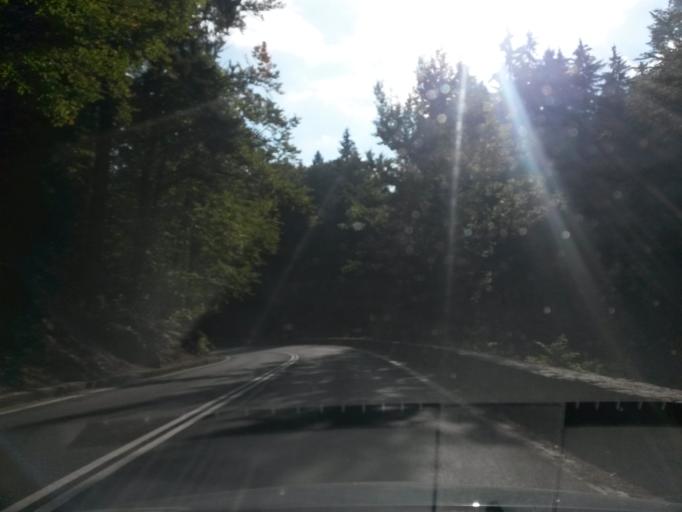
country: PL
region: Lower Silesian Voivodeship
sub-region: Powiat jeleniogorski
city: Szklarska Poreba
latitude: 50.8286
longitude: 15.5380
